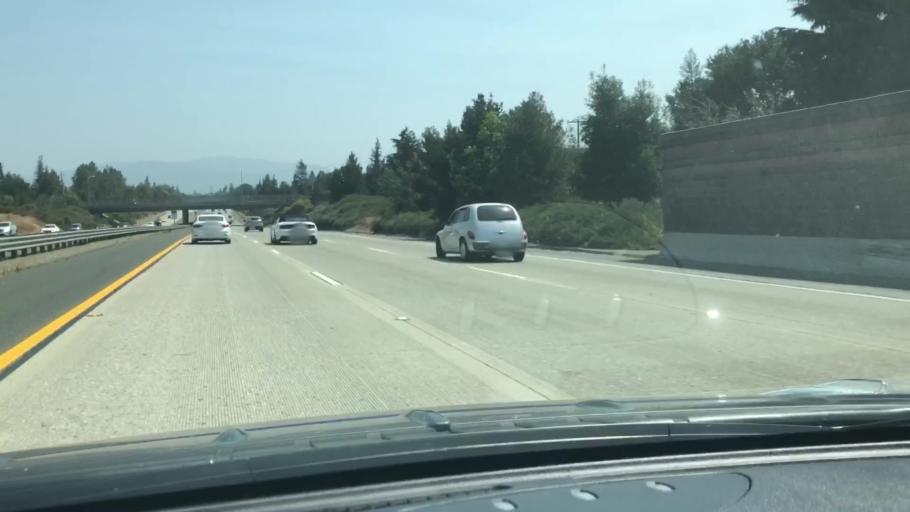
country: US
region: California
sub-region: Santa Clara County
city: Cupertino
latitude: 37.2946
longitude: -122.0284
